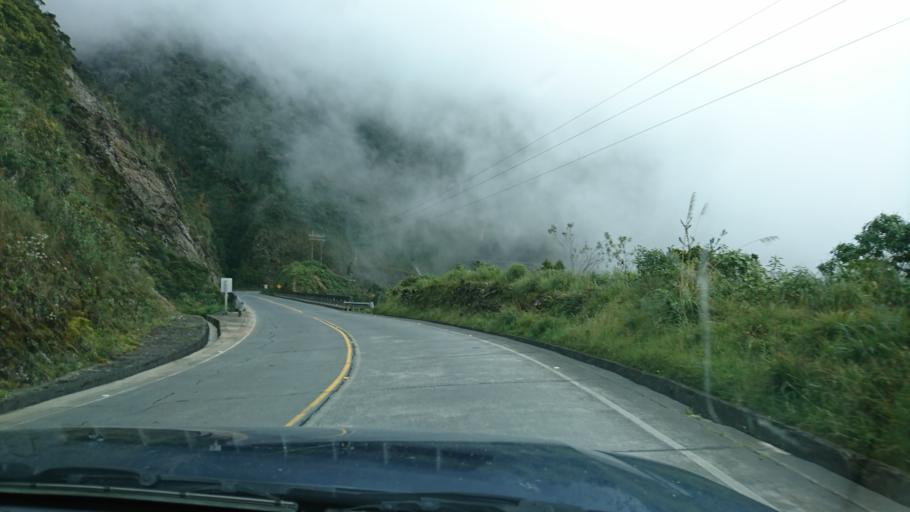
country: BO
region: La Paz
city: Coroico
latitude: -16.2701
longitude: -67.8270
